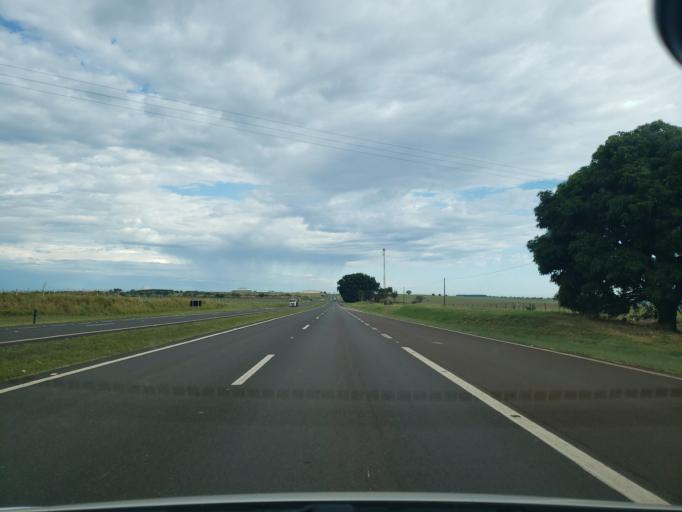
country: BR
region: Sao Paulo
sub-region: Jau
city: Jau
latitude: -22.2685
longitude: -48.4924
